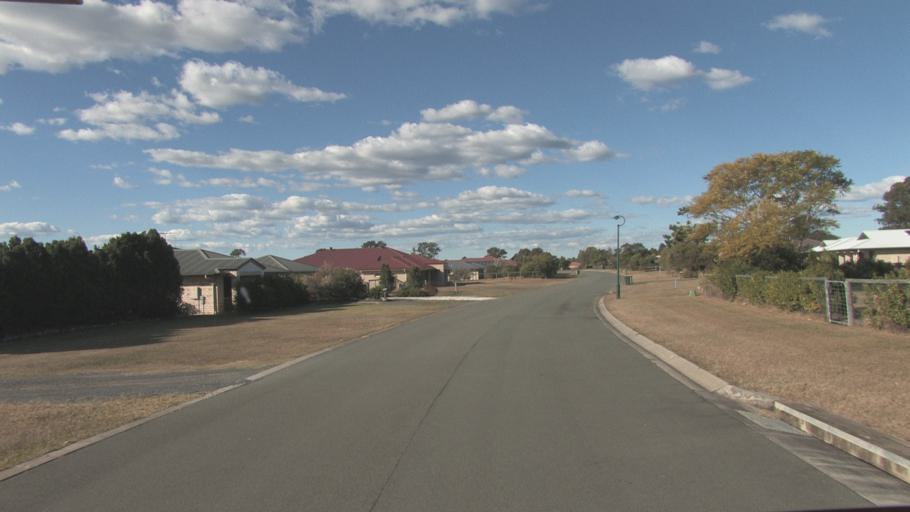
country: AU
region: Queensland
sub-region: Logan
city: North Maclean
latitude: -27.8255
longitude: 153.0037
